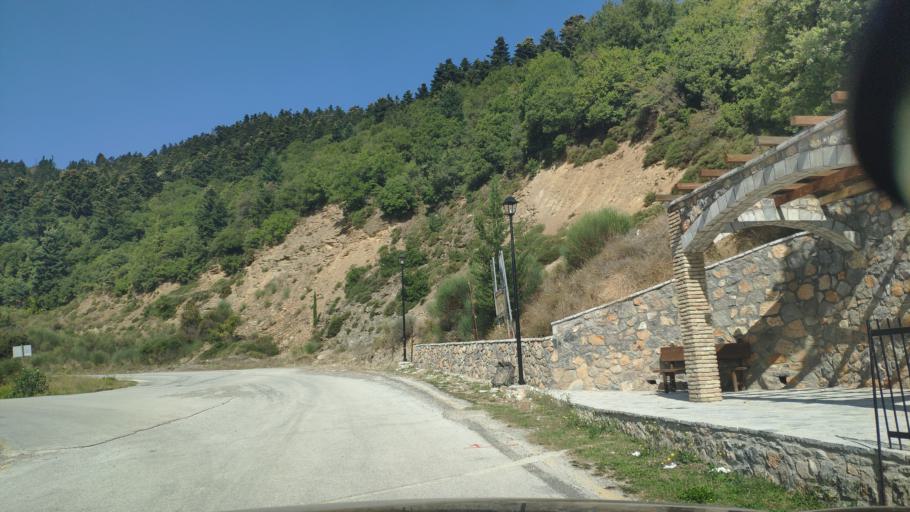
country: GR
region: West Greece
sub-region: Nomos Achaias
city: Aiyira
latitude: 37.8673
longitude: 22.3796
